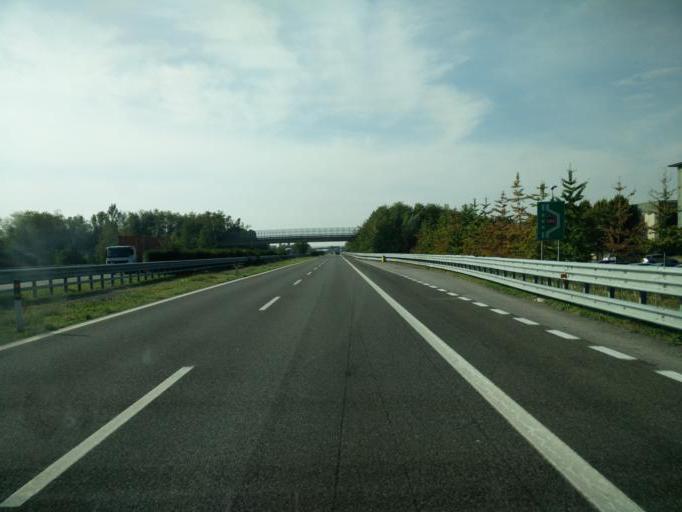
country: IT
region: Lombardy
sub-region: Provincia di Brescia
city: San Gervasio Bresciano
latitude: 45.3135
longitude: 10.1436
